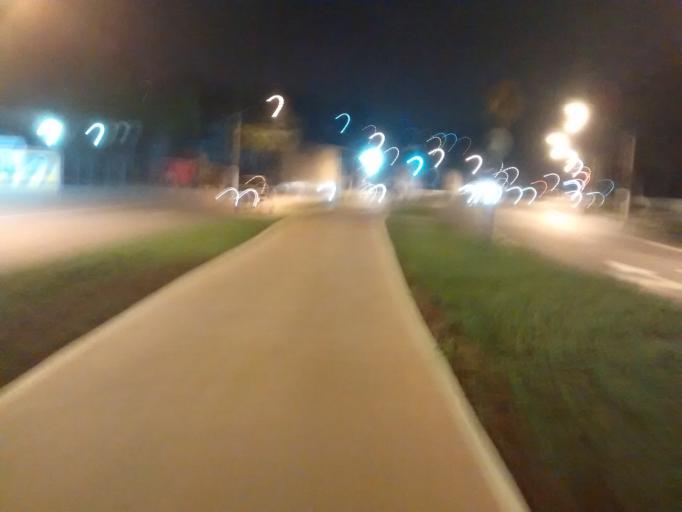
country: BR
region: Sao Paulo
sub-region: Taboao Da Serra
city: Taboao da Serra
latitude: -23.5975
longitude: -46.7471
